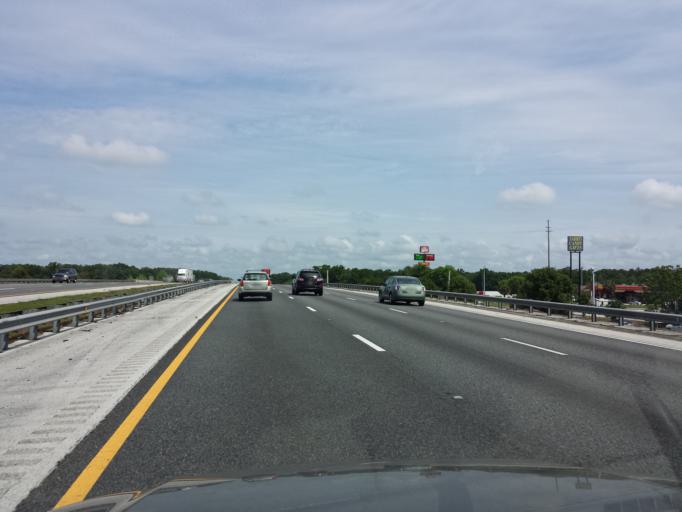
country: US
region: Florida
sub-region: Marion County
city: Ocala
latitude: 29.2652
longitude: -82.1924
